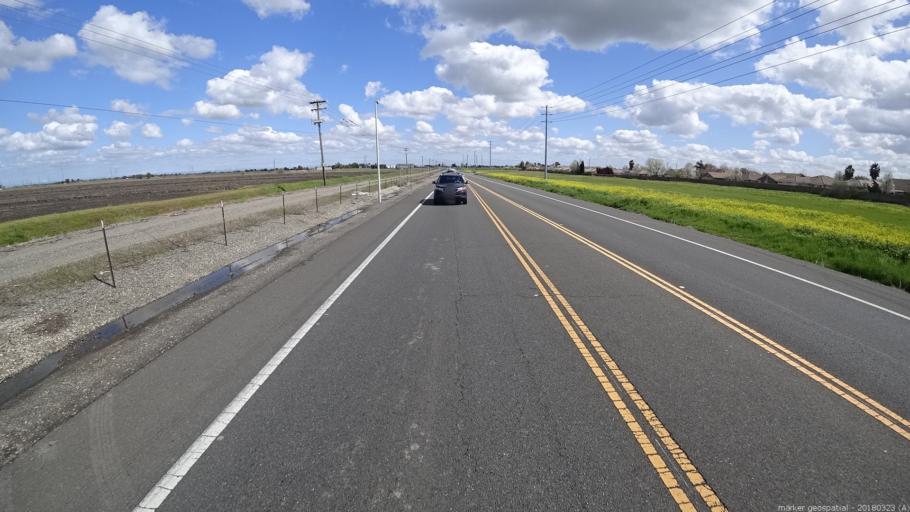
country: US
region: California
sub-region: Sacramento County
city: Elverta
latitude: 38.6852
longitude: -121.4991
